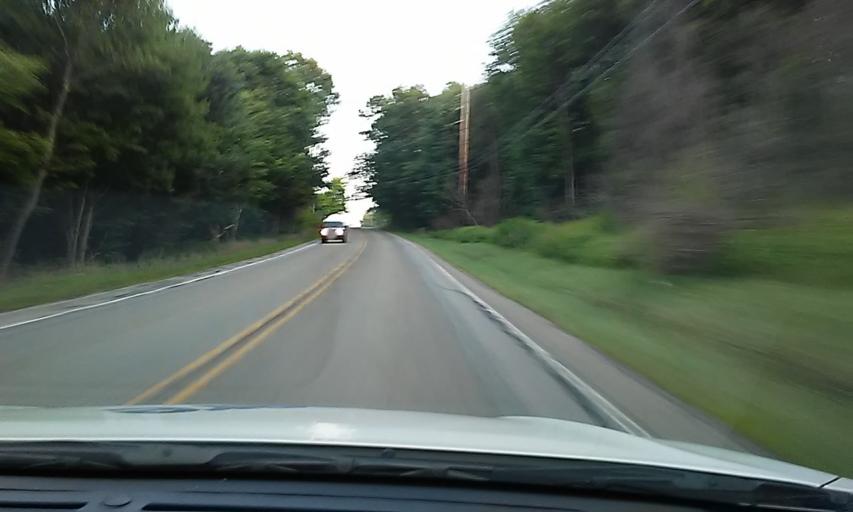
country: US
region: Pennsylvania
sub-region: Clarion County
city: Marianne
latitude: 41.2745
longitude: -79.3913
